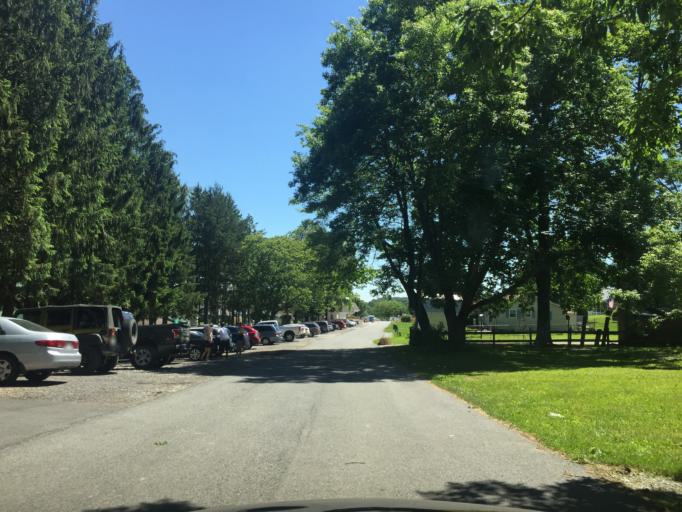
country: US
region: Maryland
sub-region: Carroll County
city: Manchester
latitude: 39.6672
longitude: -76.8773
